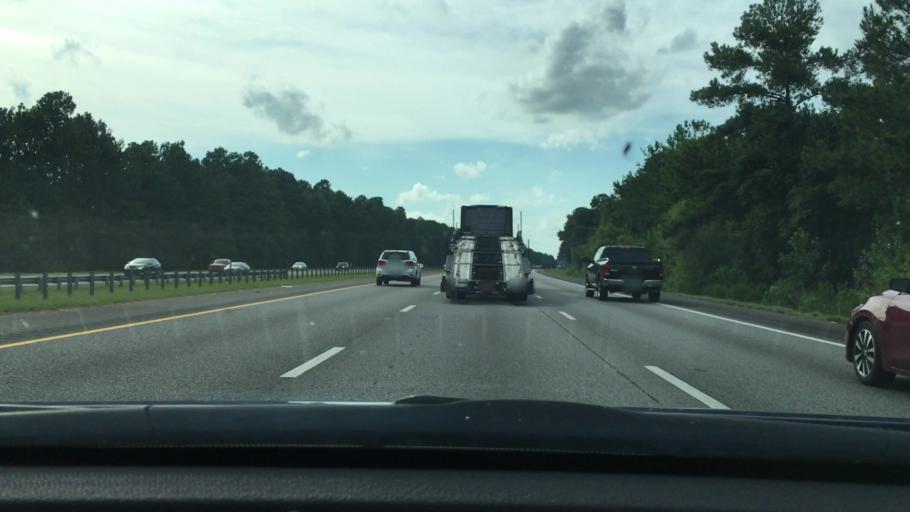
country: US
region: South Carolina
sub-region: Berkeley County
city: Sangaree
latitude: 33.0255
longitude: -80.1349
